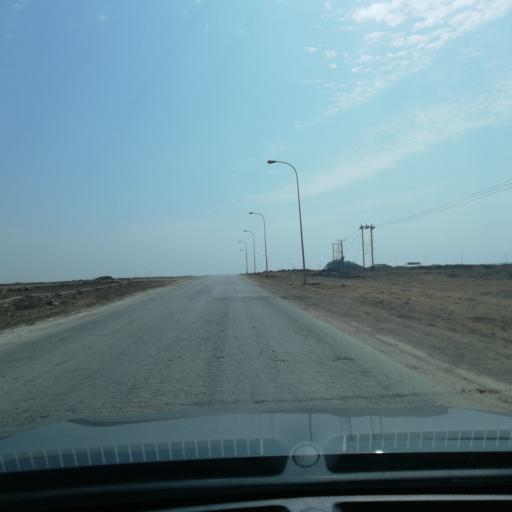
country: OM
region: Zufar
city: Salalah
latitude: 17.2432
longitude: 54.0683
